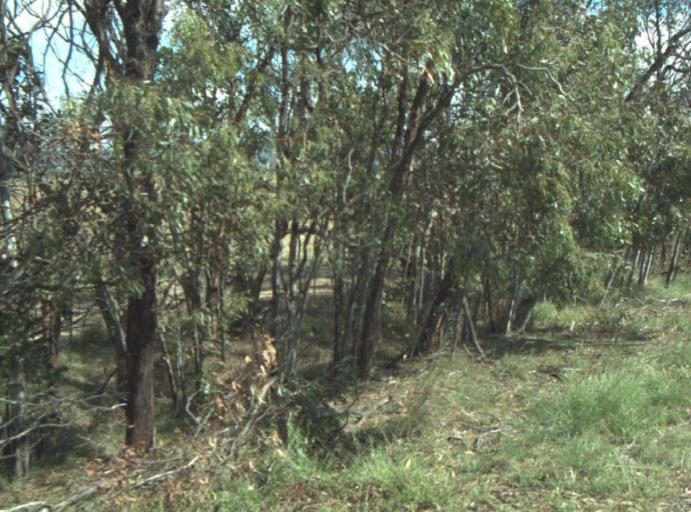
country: AU
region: Victoria
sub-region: Greater Geelong
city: Lara
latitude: -37.8563
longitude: 144.3260
